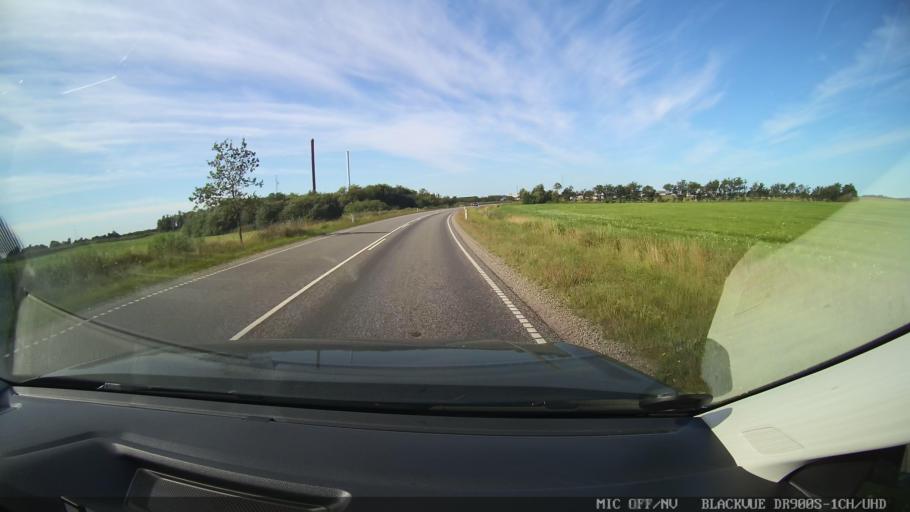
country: DK
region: North Denmark
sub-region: Mariagerfjord Kommune
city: Hobro
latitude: 56.6572
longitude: 9.8187
